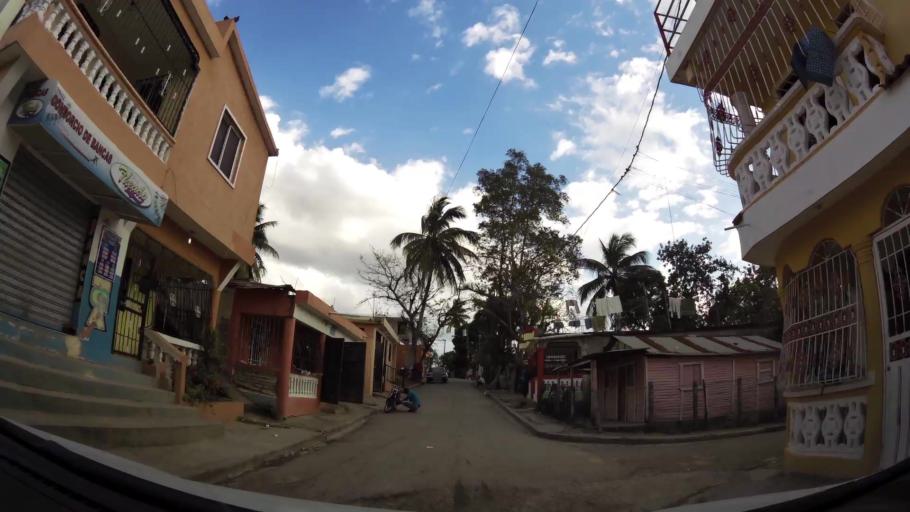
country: DO
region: Nacional
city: Ensanche Luperon
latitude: 18.5579
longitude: -69.9090
